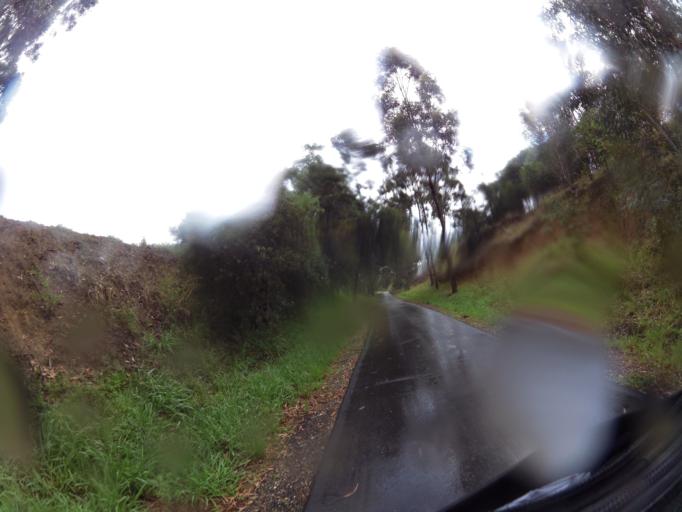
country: AU
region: Victoria
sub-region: East Gippsland
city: Bairnsdale
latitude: -37.8239
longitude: 147.6486
